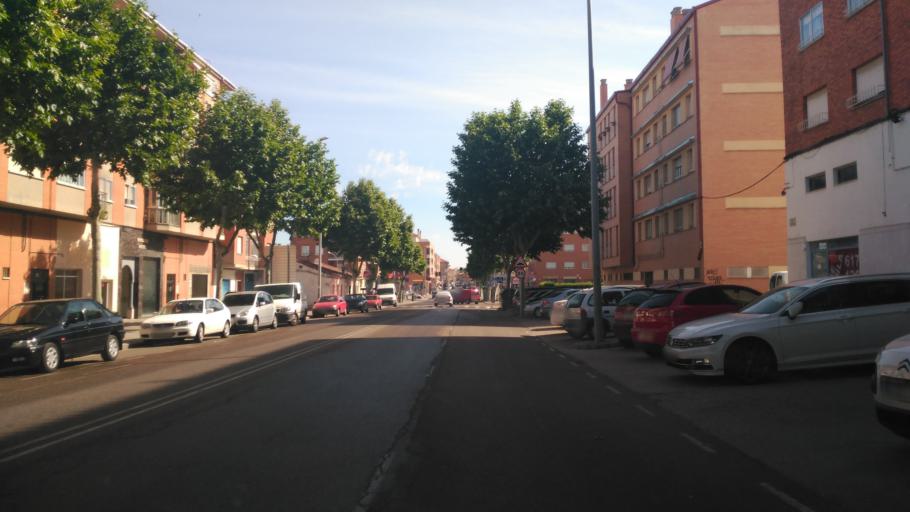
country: ES
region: Castille and Leon
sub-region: Provincia de Zamora
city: Zamora
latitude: 41.4934
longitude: -5.7422
